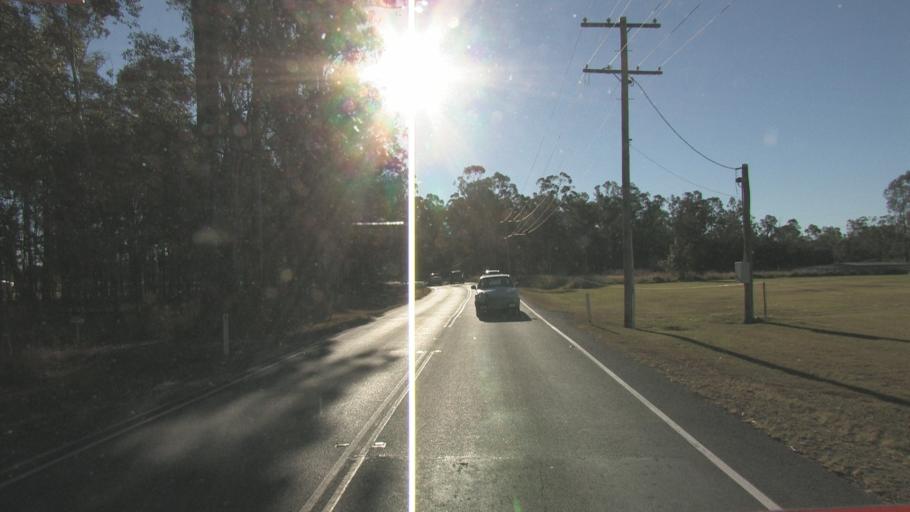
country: AU
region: Queensland
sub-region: Logan
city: Chambers Flat
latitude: -27.7474
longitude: 153.0745
